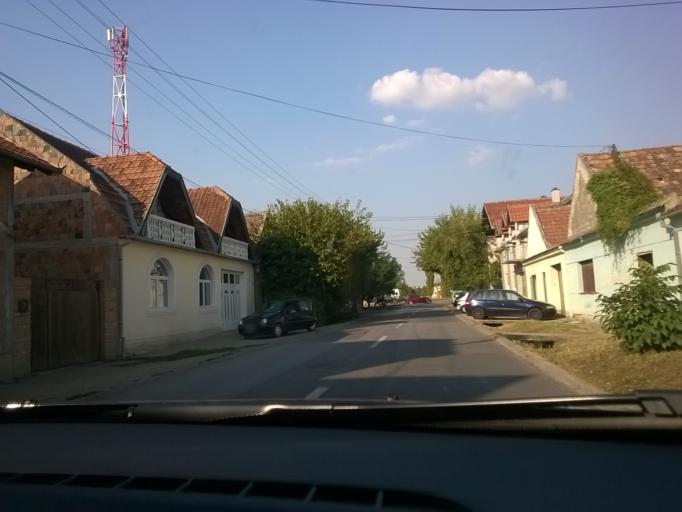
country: RS
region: Autonomna Pokrajina Vojvodina
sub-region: Juznobanatski Okrug
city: Vrsac
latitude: 45.1257
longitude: 21.2857
